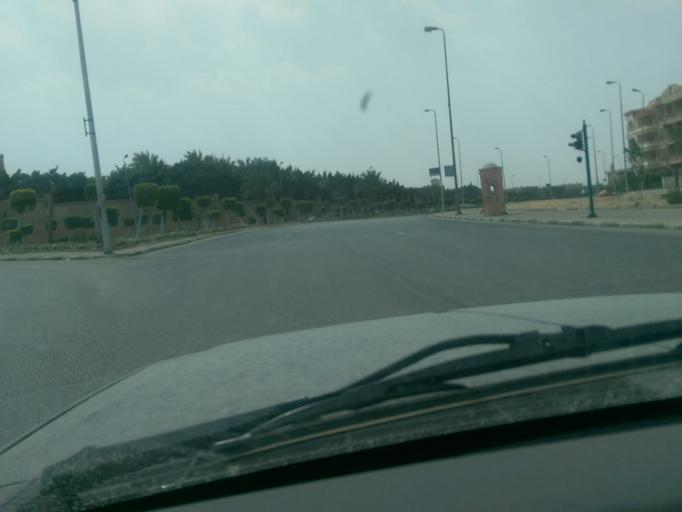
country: EG
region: Muhafazat al Qahirah
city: Cairo
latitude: 29.9902
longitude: 31.4308
